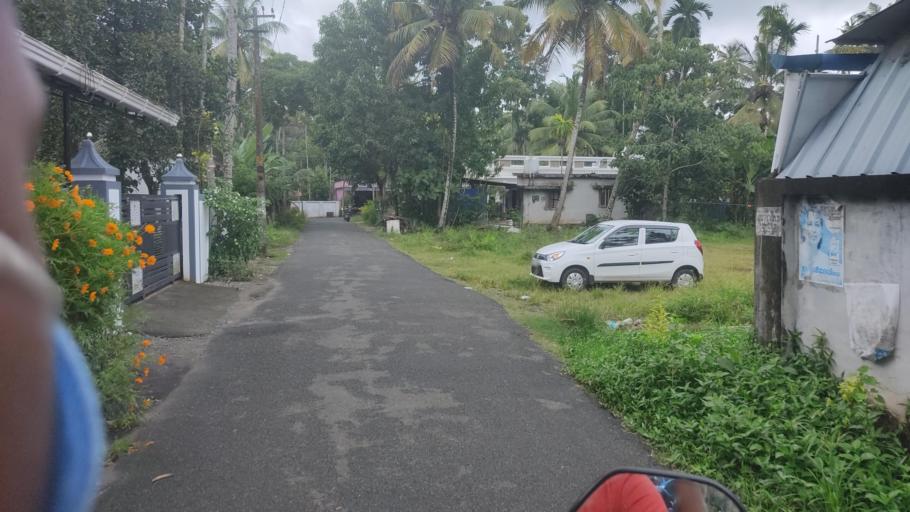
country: IN
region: Kerala
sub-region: Alappuzha
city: Kayankulam
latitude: 9.1638
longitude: 76.4890
